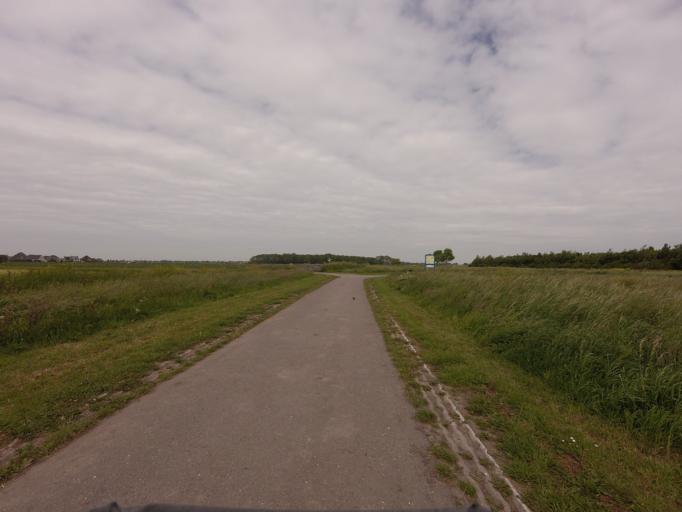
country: NL
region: North Holland
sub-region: Gemeente Medemblik
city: Opperdoes
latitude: 52.7114
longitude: 5.1061
